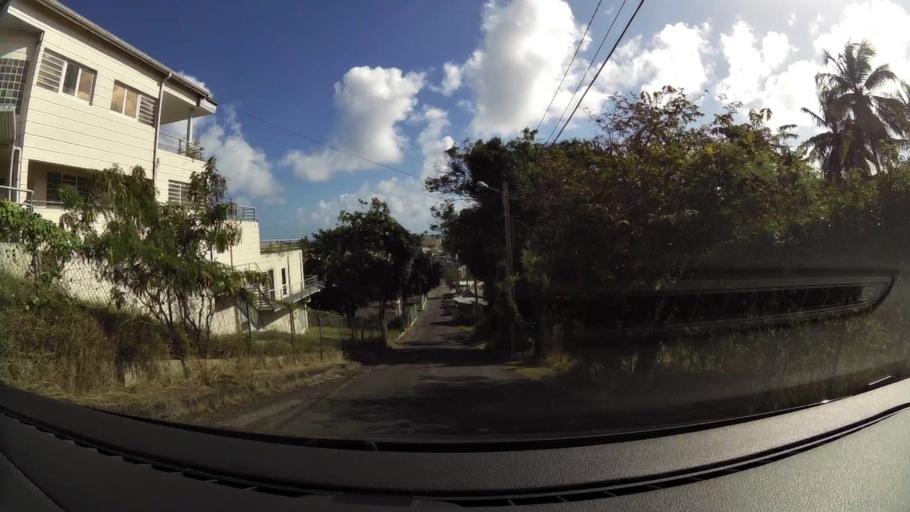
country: GP
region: Guadeloupe
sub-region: Guadeloupe
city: Sainte-Anne
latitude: 16.2278
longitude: -61.3837
